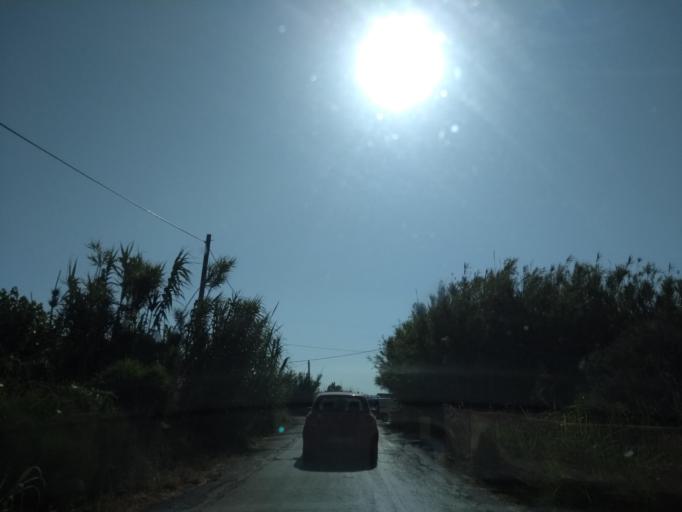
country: GR
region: Crete
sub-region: Nomos Chanias
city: Georgioupolis
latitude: 35.3471
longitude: 24.2937
